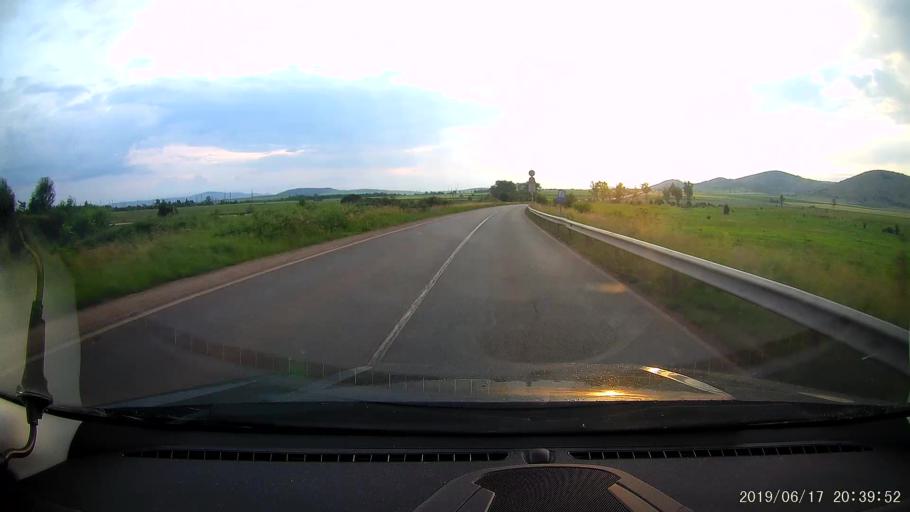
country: BG
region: Sofiya
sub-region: Obshtina Slivnitsa
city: Slivnitsa
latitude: 42.8822
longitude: 22.9970
